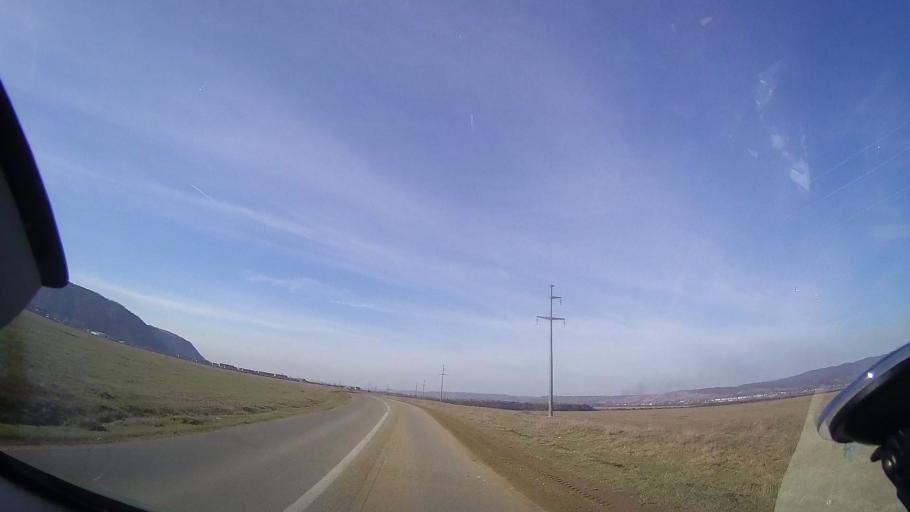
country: RO
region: Bihor
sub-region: Comuna Magesti
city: Magesti
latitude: 47.0214
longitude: 22.4180
